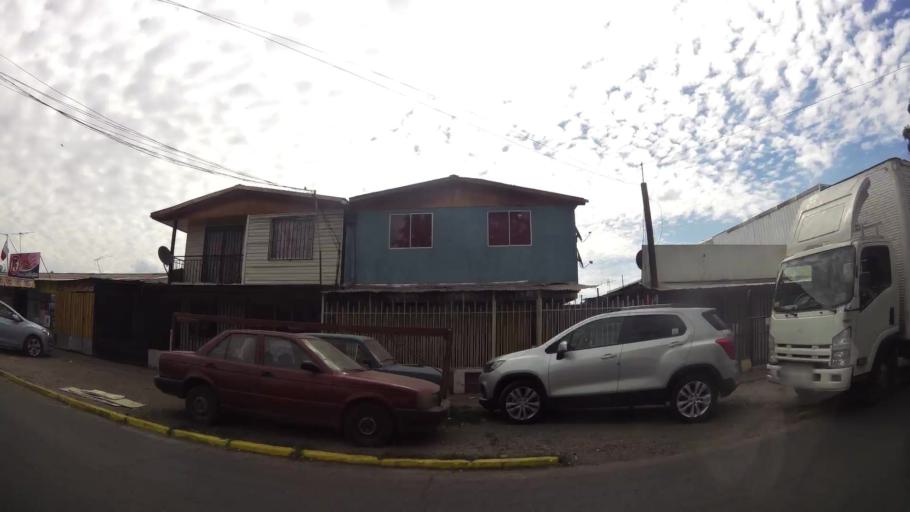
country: CL
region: Santiago Metropolitan
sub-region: Provincia de Santiago
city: La Pintana
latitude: -33.5768
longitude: -70.6384
